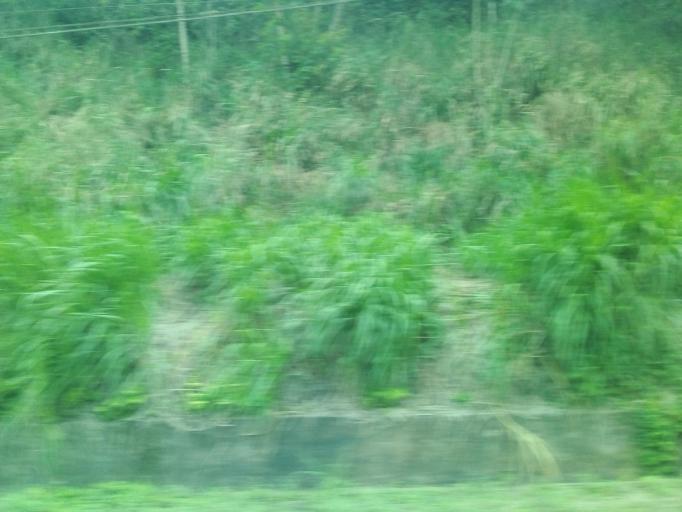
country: BR
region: Minas Gerais
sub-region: Nova Era
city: Nova Era
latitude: -19.7317
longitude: -43.0000
